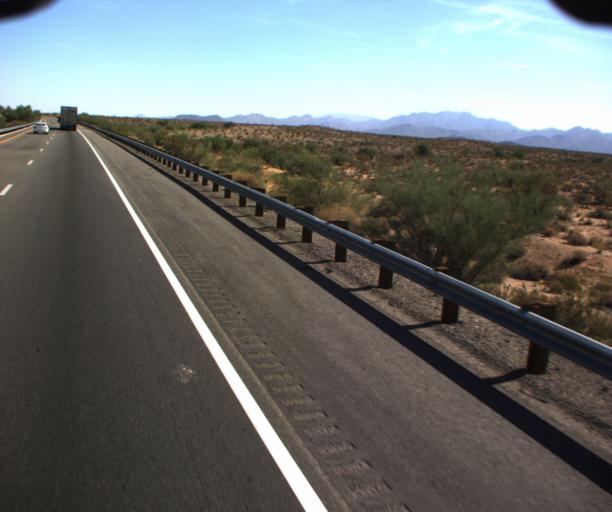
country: US
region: Arizona
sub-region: Mohave County
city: Desert Hills
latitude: 34.8168
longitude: -114.1460
